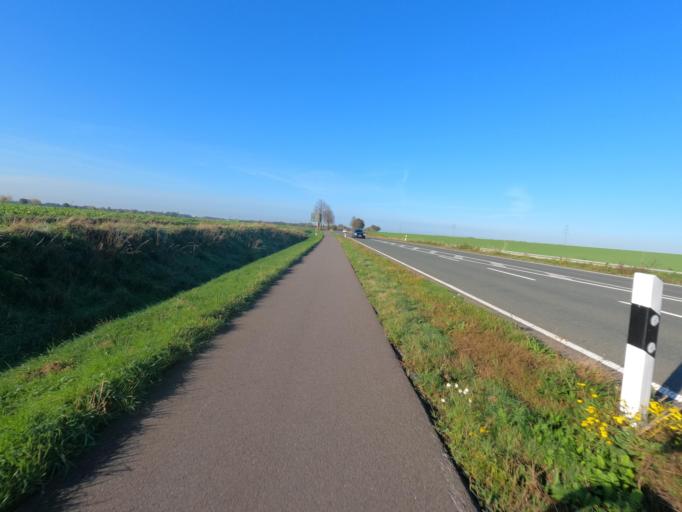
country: DE
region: North Rhine-Westphalia
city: Erkelenz
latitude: 51.0821
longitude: 6.3630
